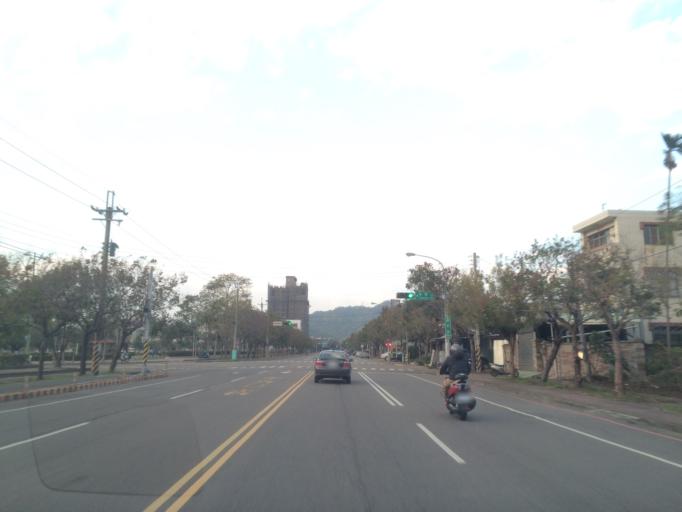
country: TW
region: Taiwan
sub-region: Taichung City
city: Taichung
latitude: 24.1661
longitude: 120.7334
